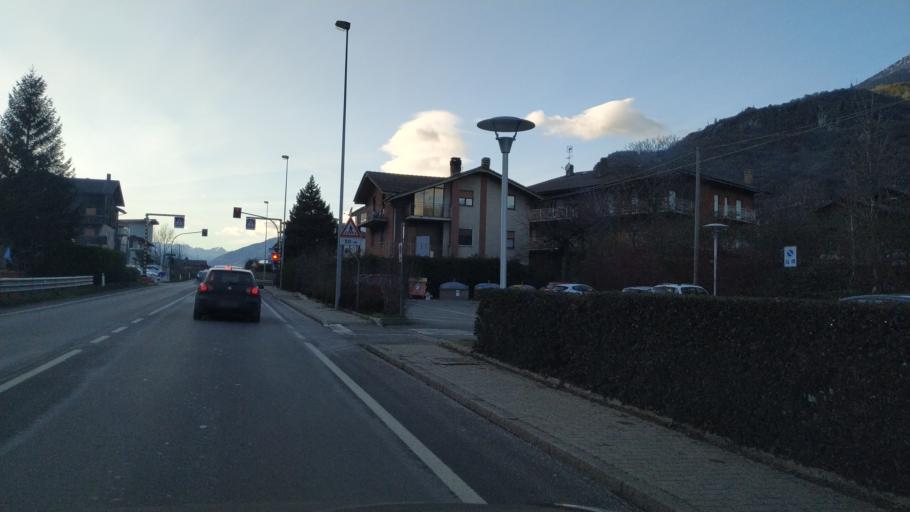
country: IT
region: Aosta Valley
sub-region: Valle d'Aosta
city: Nus
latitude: 45.7388
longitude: 7.4668
